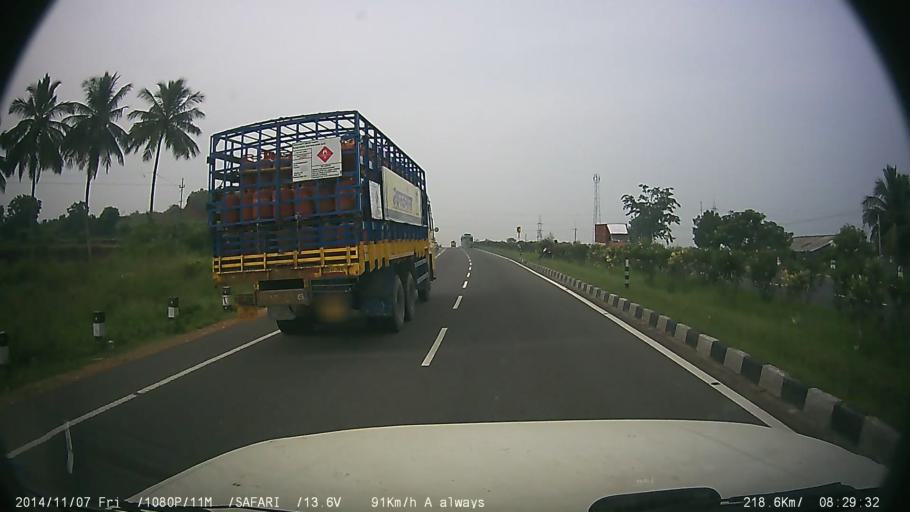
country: IN
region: Tamil Nadu
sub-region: Salem
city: Attayyampatti
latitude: 11.5760
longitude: 78.0422
